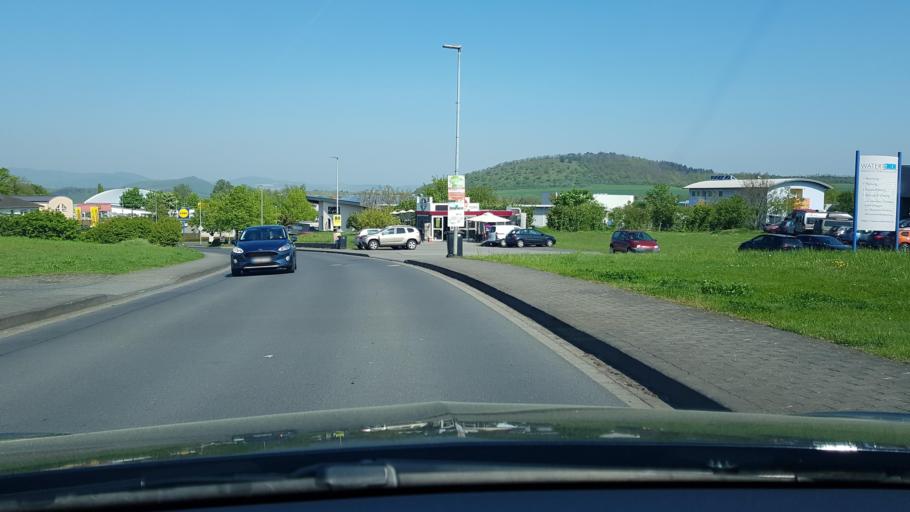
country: DE
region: Rheinland-Pfalz
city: Ochtendung
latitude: 50.3515
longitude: 7.3975
